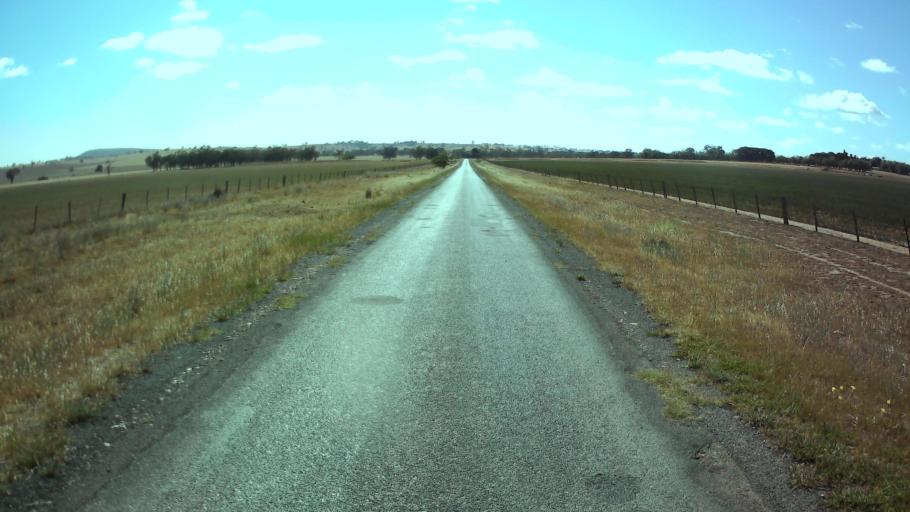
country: AU
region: New South Wales
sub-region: Young
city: Young
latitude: -34.0754
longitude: 148.3547
